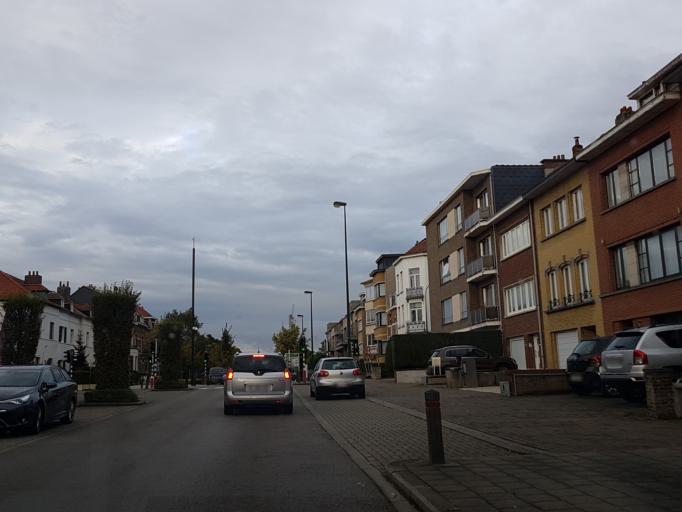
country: BE
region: Flanders
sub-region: Provincie Vlaams-Brabant
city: Kraainem
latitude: 50.8329
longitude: 4.4468
